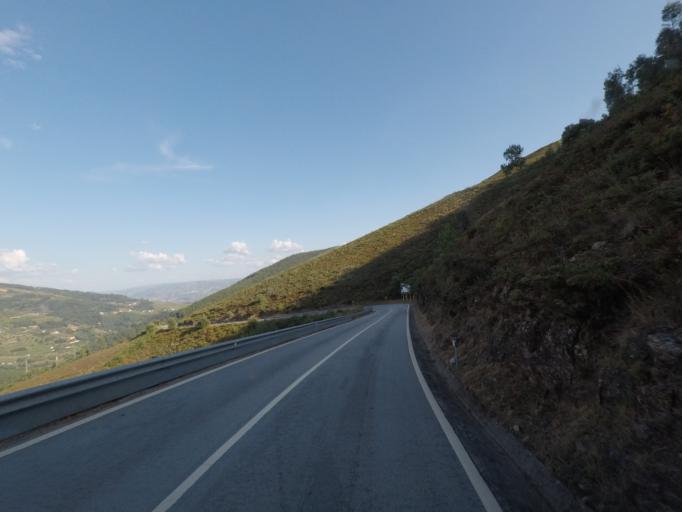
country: PT
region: Vila Real
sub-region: Mesao Frio
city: Mesao Frio
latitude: 41.1786
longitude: -7.9306
